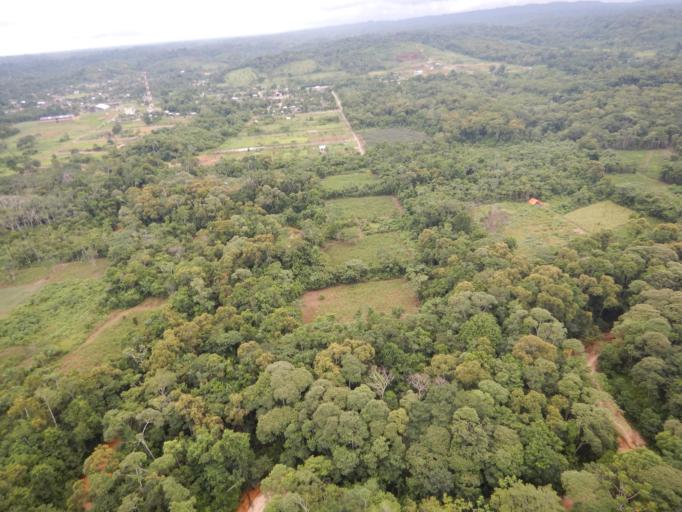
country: BO
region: Cochabamba
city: Chimore
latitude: -17.0054
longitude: -65.0065
